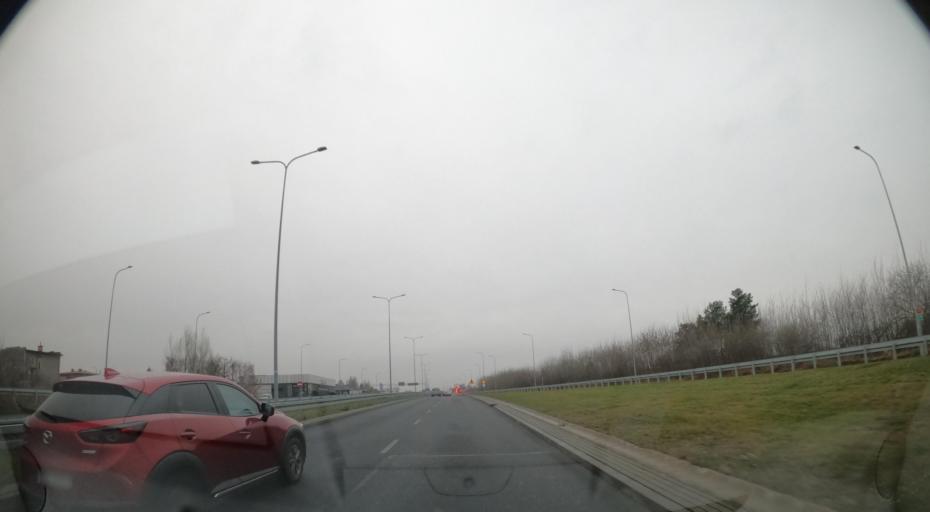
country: PL
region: Masovian Voivodeship
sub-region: Radom
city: Radom
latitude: 51.3955
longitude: 21.1964
